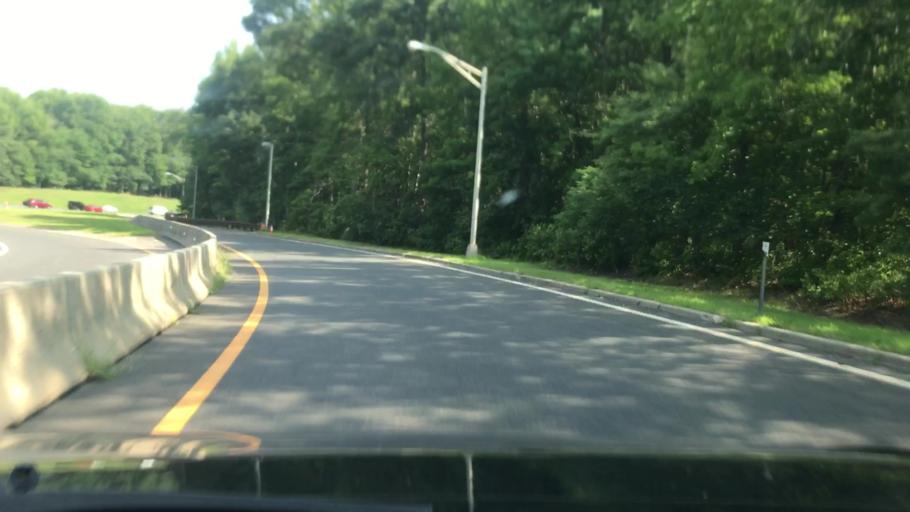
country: US
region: New Jersey
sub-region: Monmouth County
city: Shark River Hills
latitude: 40.2129
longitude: -74.1007
